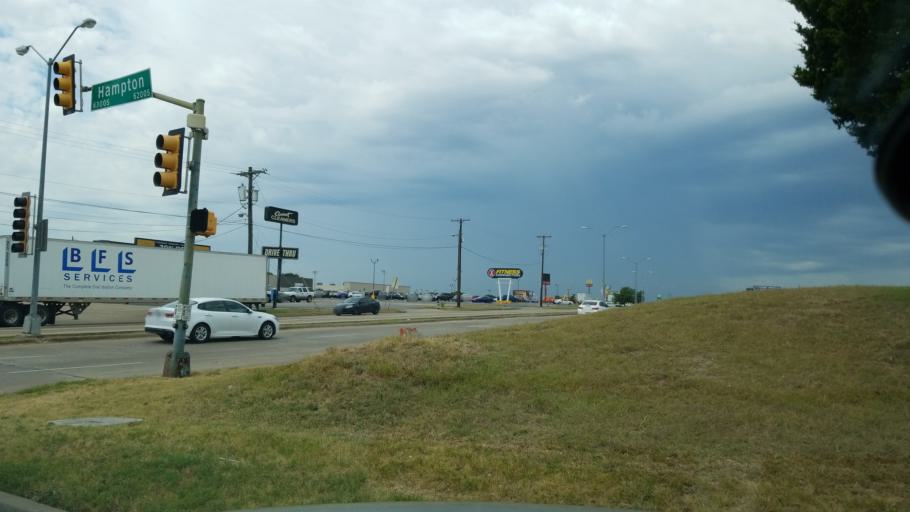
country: US
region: Texas
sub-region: Dallas County
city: Duncanville
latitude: 32.6719
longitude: -96.8572
